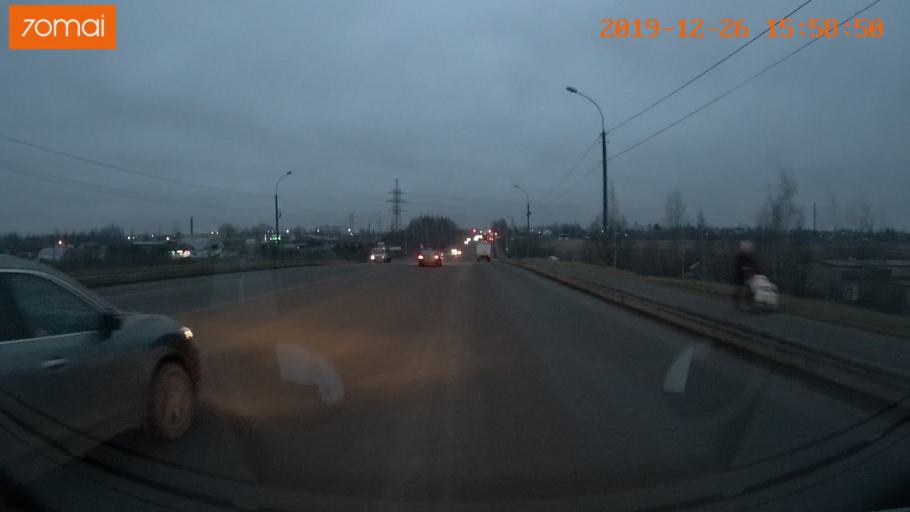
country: RU
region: Jaroslavl
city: Rybinsk
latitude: 58.0361
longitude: 38.7992
